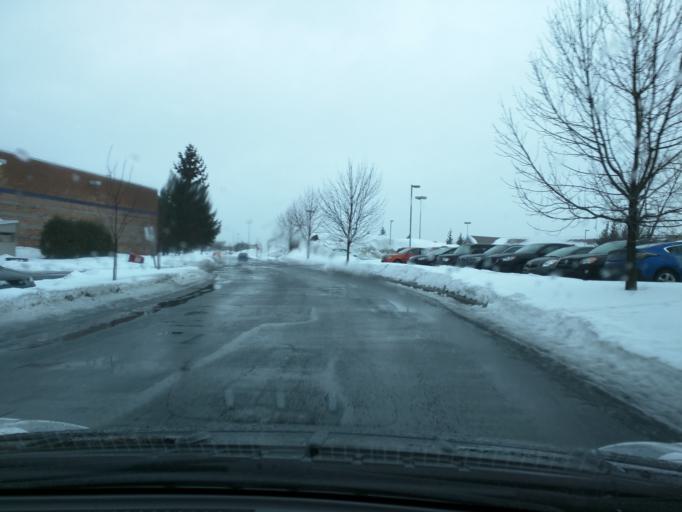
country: CA
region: Quebec
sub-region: Monteregie
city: Longueuil
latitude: 45.5375
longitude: -73.4658
